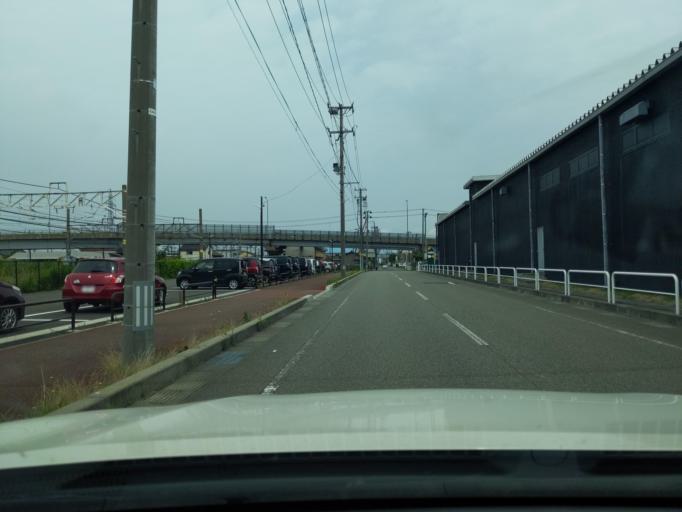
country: JP
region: Niigata
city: Kashiwazaki
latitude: 37.3641
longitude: 138.5620
